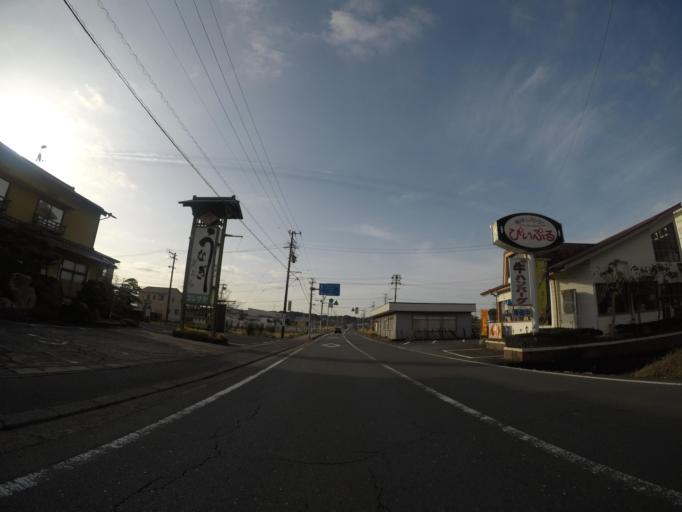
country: JP
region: Shizuoka
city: Hamakita
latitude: 34.8164
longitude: 137.6844
